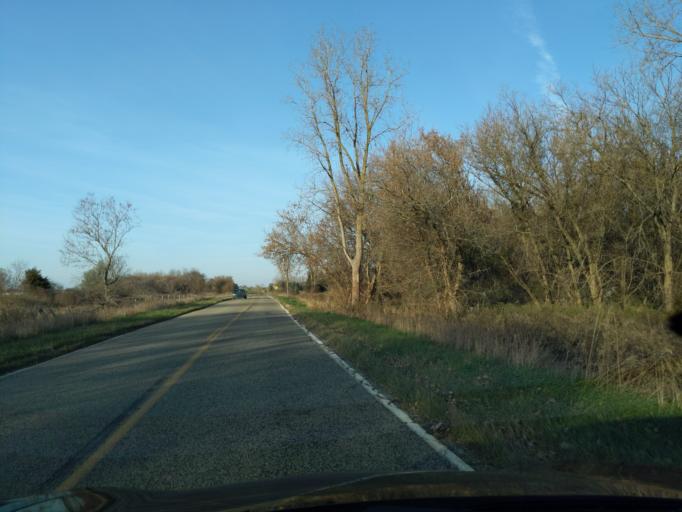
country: US
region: Michigan
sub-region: Ingham County
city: East Lansing
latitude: 42.7959
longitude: -84.5112
